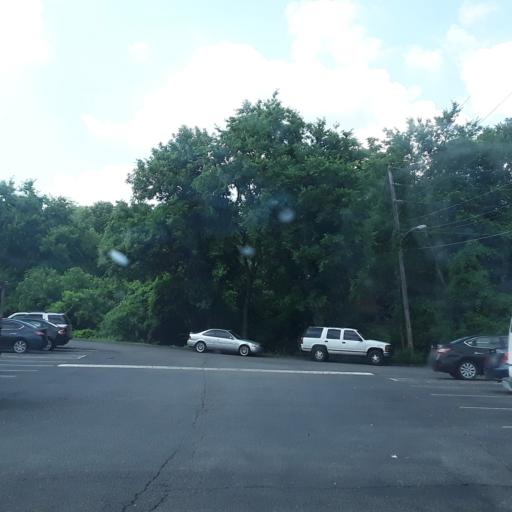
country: US
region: Tennessee
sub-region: Davidson County
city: Oak Hill
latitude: 36.1138
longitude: -86.7353
